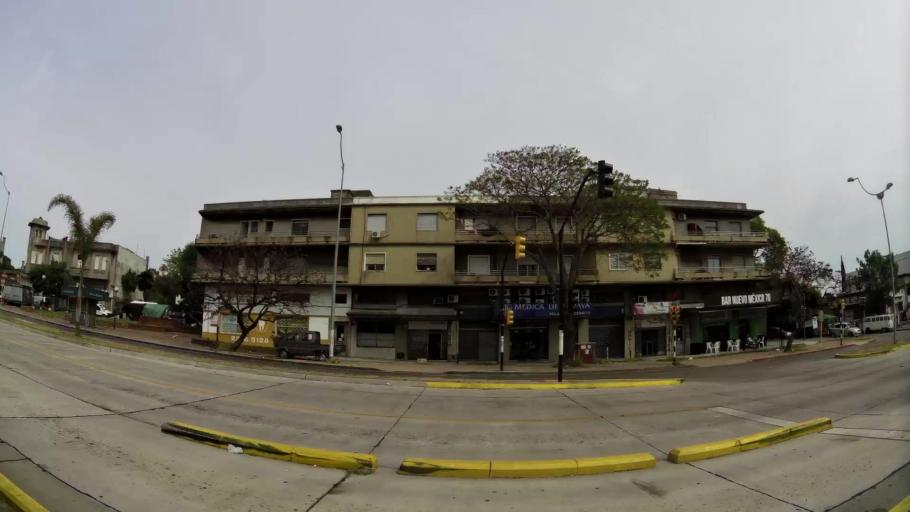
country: UY
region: Montevideo
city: Montevideo
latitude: -34.8533
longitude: -56.1610
